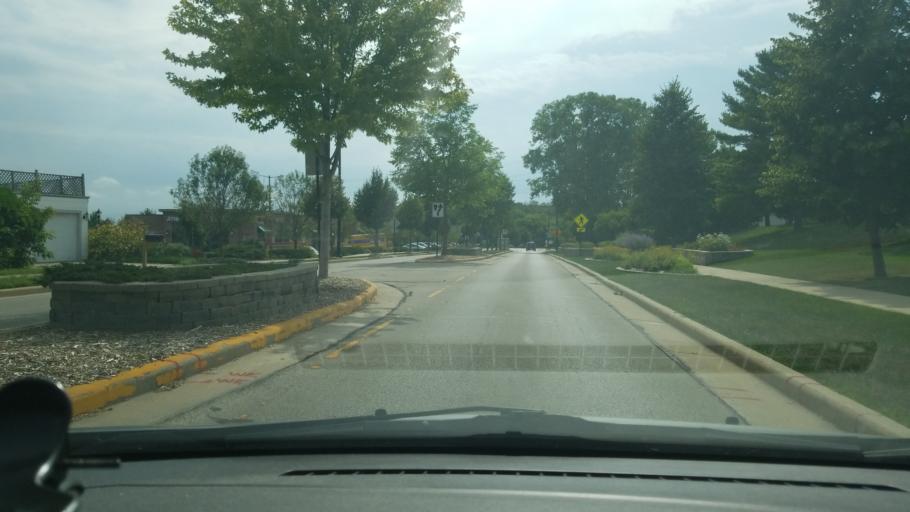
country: US
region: Wisconsin
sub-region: Ozaukee County
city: Grafton
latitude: 43.3030
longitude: -87.9627
